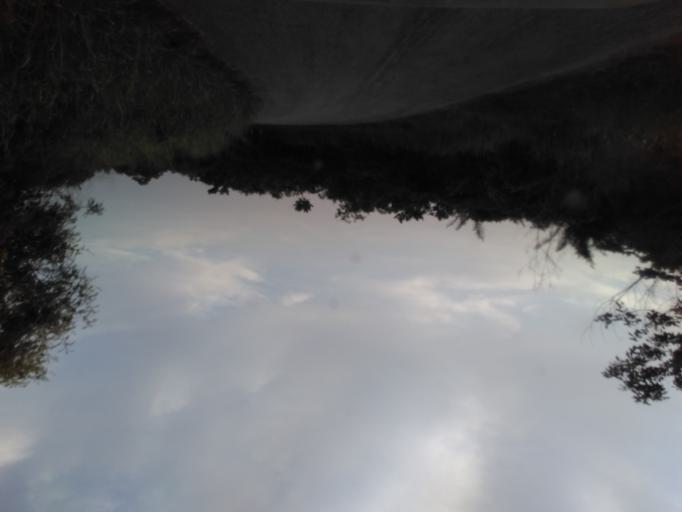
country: GH
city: Bekwai
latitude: 6.5492
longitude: -1.4373
